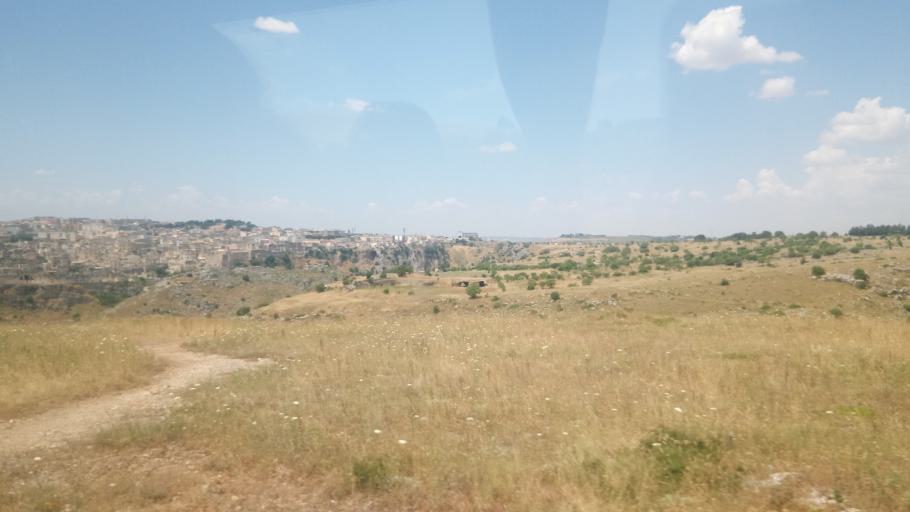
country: IT
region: Basilicate
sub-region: Provincia di Matera
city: Matera
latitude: 40.6694
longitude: 16.6238
